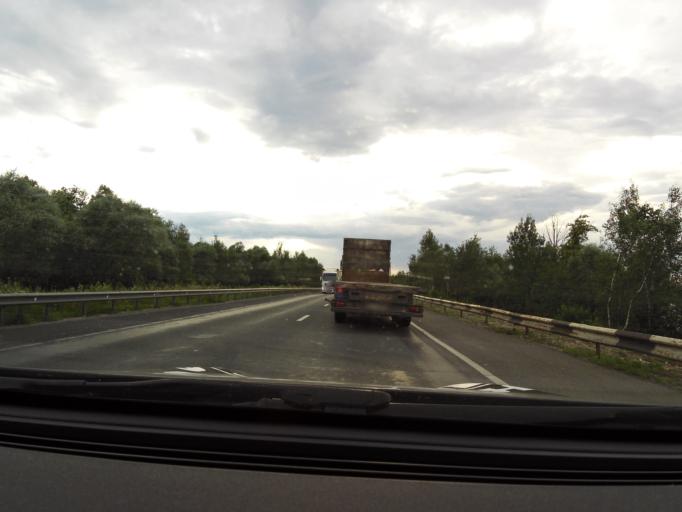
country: RU
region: Vladimir
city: Raduzhnyy
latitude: 56.0575
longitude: 40.3907
